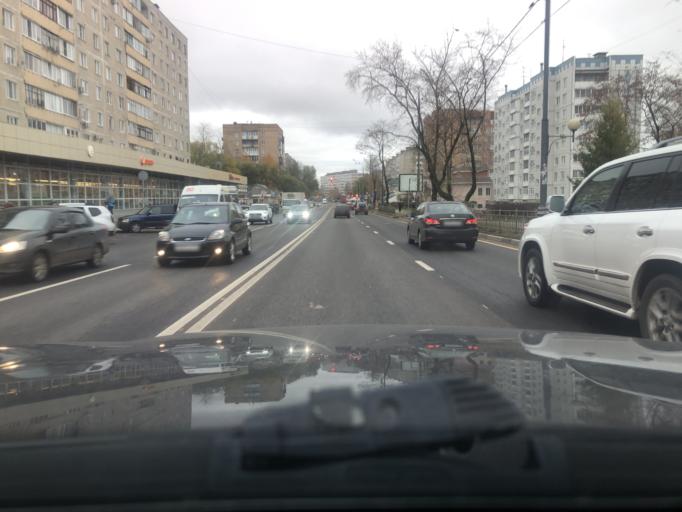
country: RU
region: Moskovskaya
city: Sergiyev Posad
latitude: 56.3268
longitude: 38.1327
